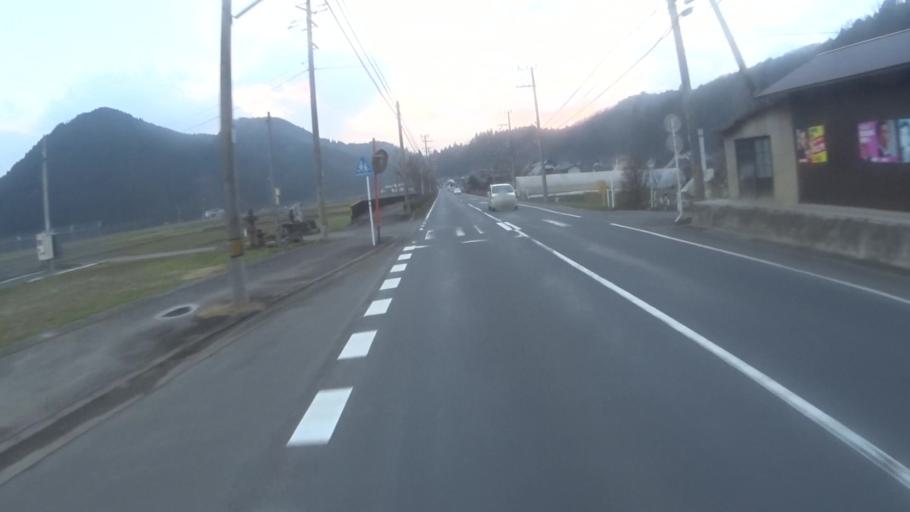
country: JP
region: Kyoto
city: Ayabe
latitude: 35.3286
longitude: 135.3351
